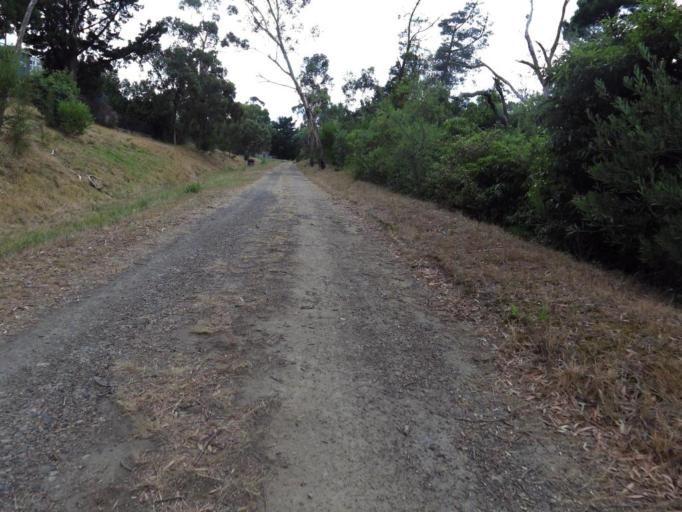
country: AU
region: Victoria
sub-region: Frankston
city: Frankston South
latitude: -38.1805
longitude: 145.1352
